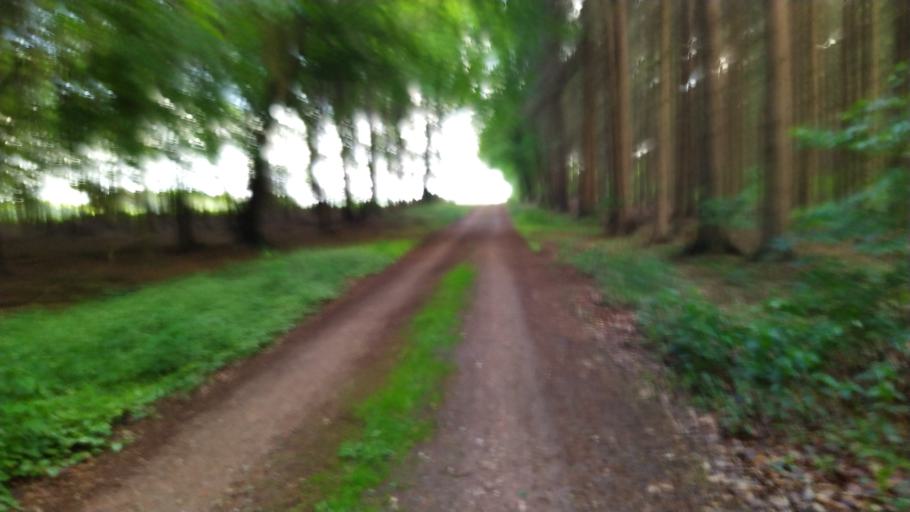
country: DE
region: Lower Saxony
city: Farven
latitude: 53.4399
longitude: 9.2985
